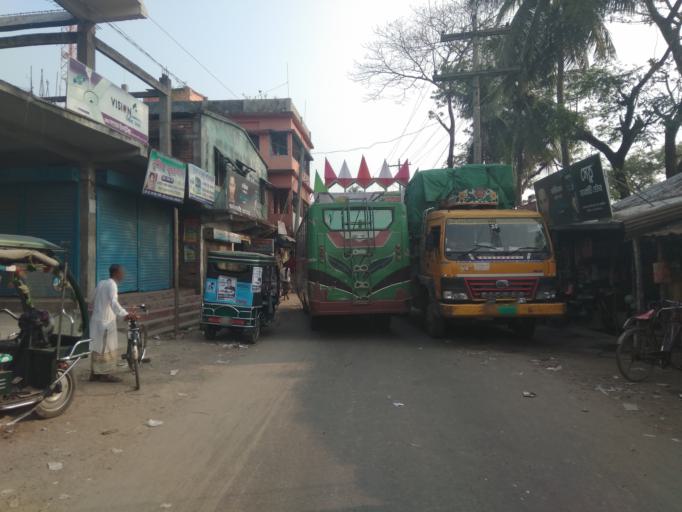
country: BD
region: Khulna
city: Kesabpur
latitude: 22.7500
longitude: 89.2563
